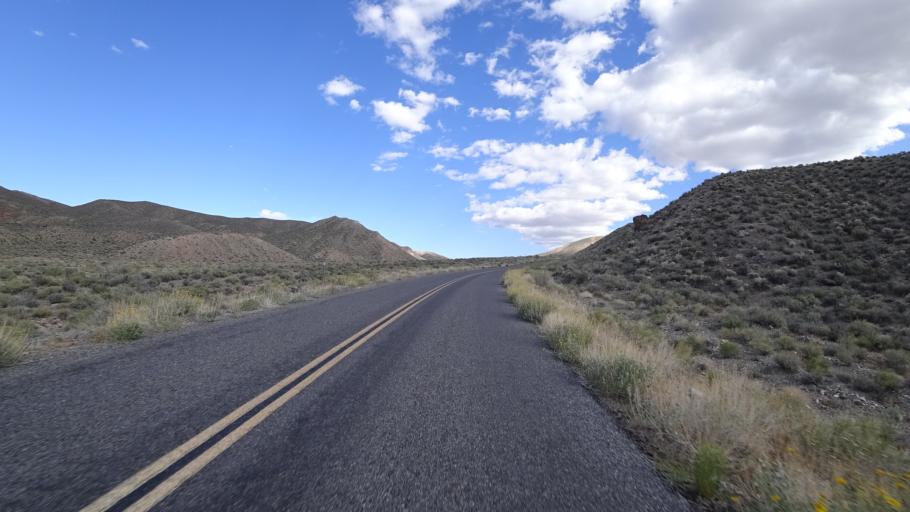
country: US
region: Nevada
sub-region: Nye County
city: Beatty
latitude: 36.4135
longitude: -117.1776
